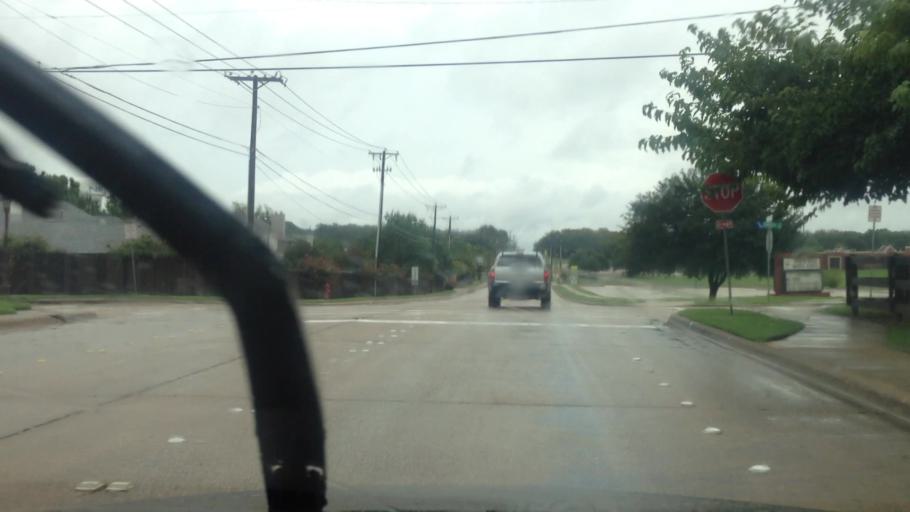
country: US
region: Texas
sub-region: Tarrant County
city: Watauga
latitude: 32.8822
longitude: -97.2253
